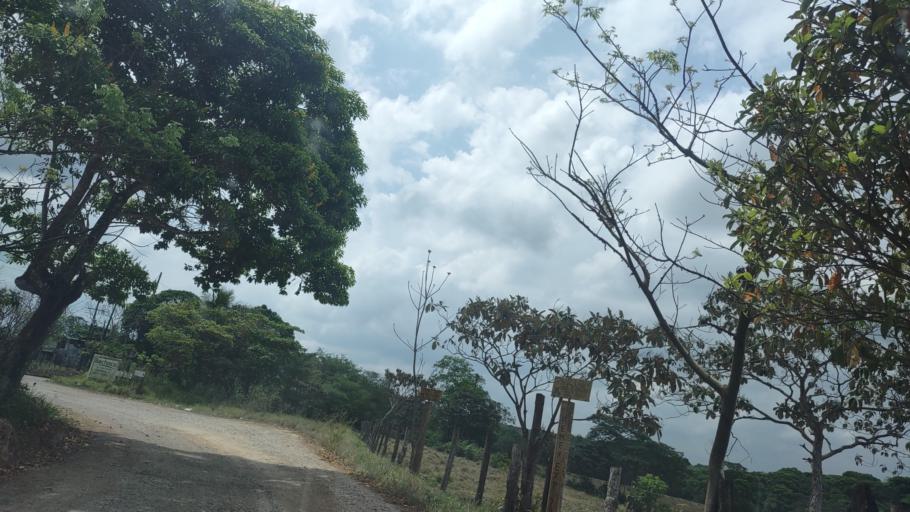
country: MX
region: Veracruz
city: Las Choapas
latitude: 17.9565
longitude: -94.1111
